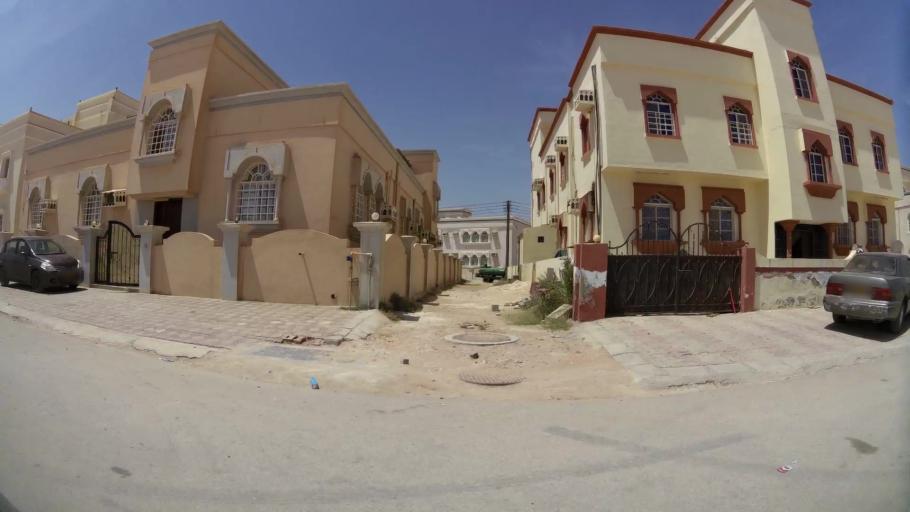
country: OM
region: Zufar
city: Salalah
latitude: 17.0609
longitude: 54.1608
